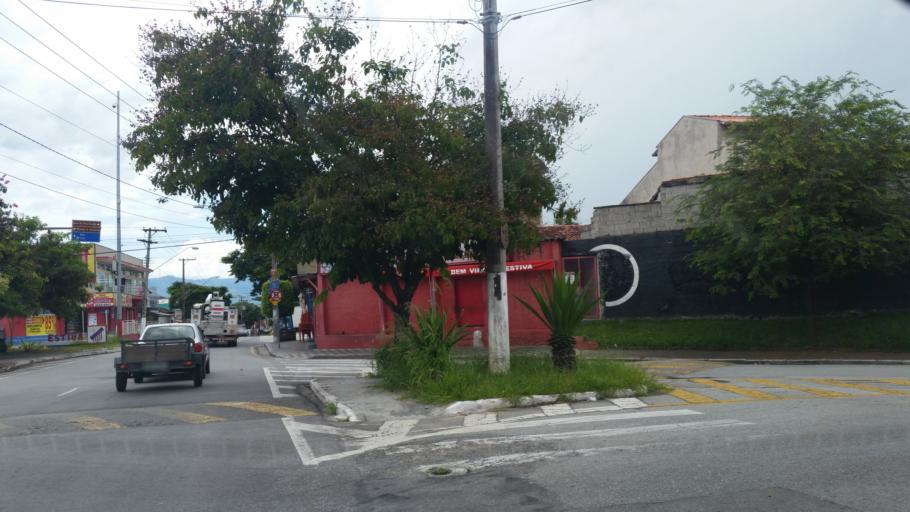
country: BR
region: Sao Paulo
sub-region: Taubate
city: Taubate
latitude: -23.0221
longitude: -45.5707
